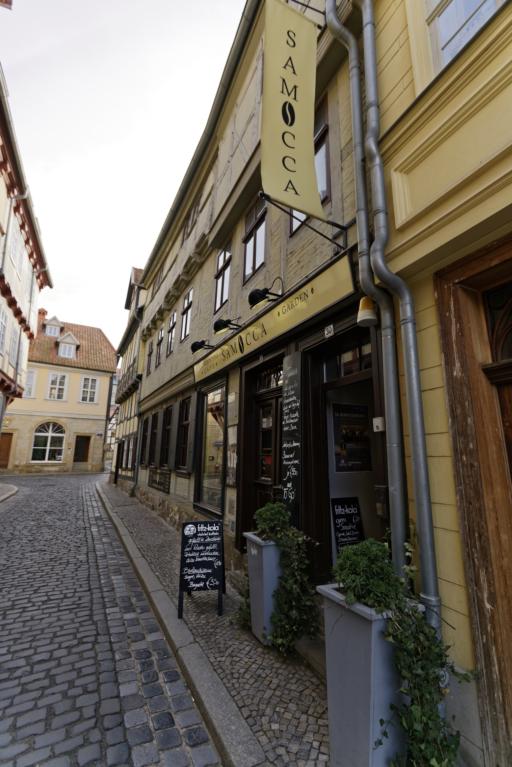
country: DE
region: Saxony-Anhalt
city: Quedlinburg
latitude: 51.7877
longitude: 11.1375
